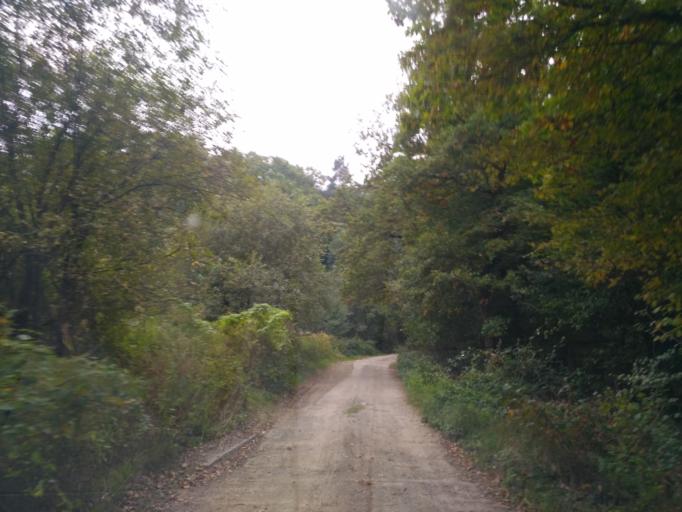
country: SK
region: Kosicky
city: Kosice
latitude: 48.7948
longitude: 21.2734
